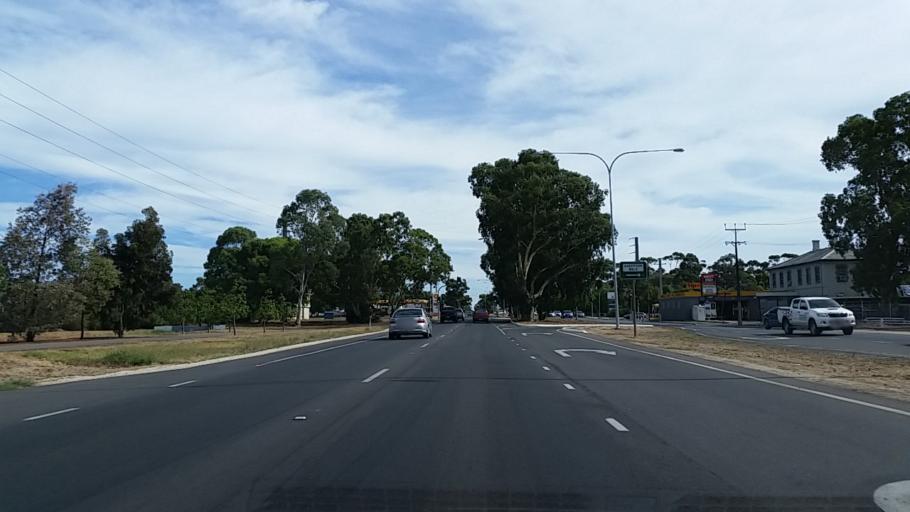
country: AU
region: South Australia
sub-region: Playford
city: Smithfield
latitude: -34.6827
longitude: 138.6940
